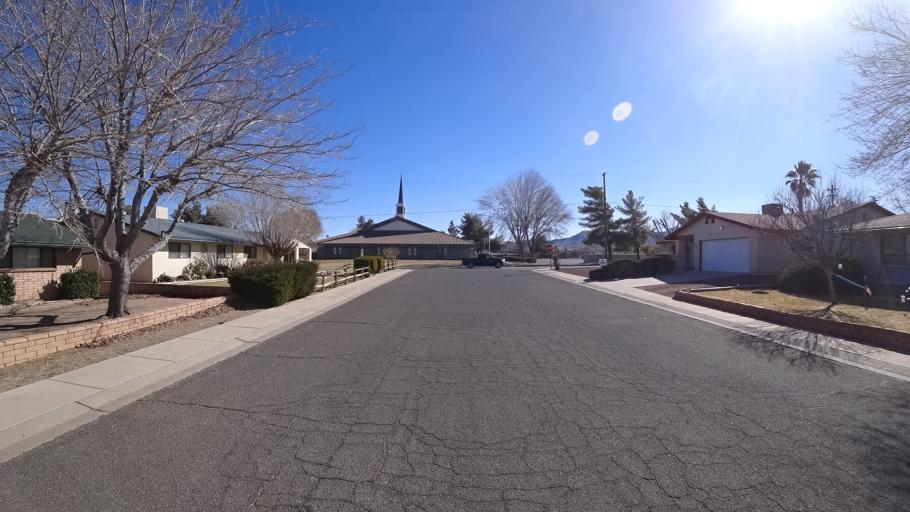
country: US
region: Arizona
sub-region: Mohave County
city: Kingman
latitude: 35.1949
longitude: -114.0120
